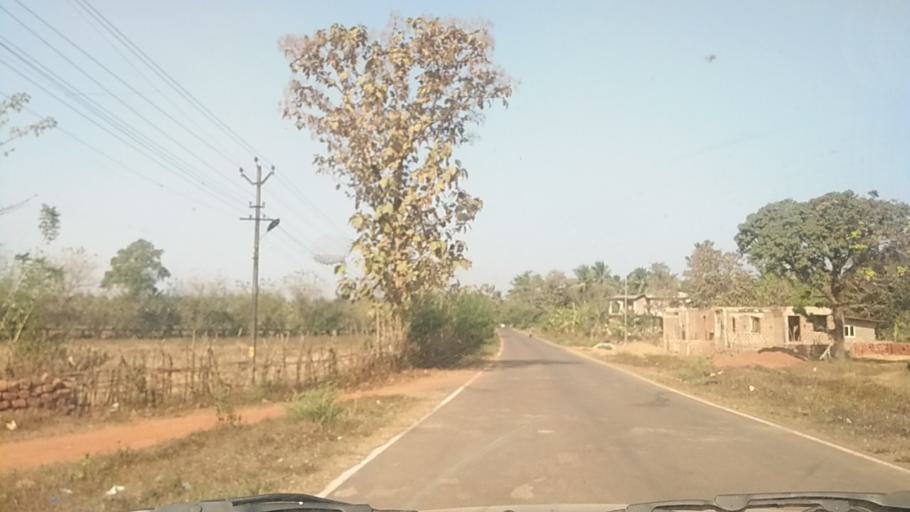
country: IN
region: Goa
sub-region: South Goa
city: Sanguem
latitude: 15.2288
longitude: 74.1845
